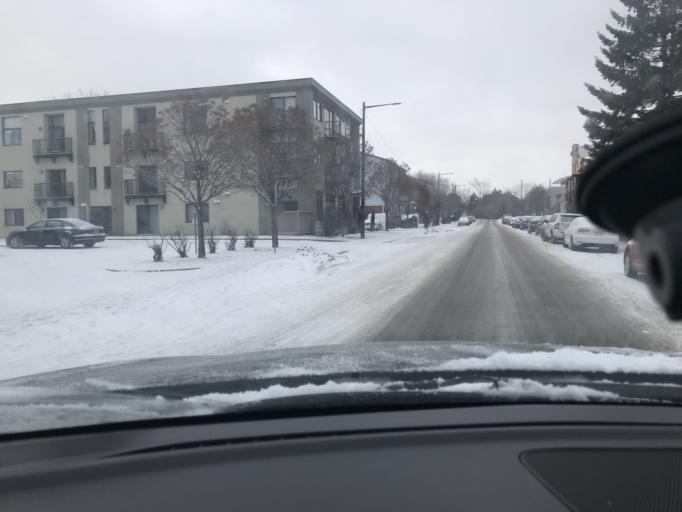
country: CA
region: Quebec
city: Quebec
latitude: 46.8209
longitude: -71.2221
